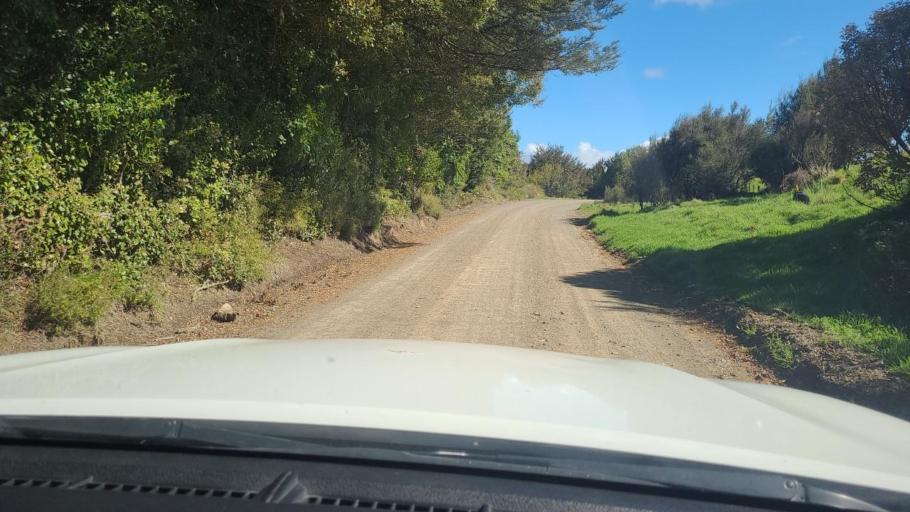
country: NZ
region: Hawke's Bay
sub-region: Napier City
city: Napier
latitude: -39.1195
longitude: 176.8101
